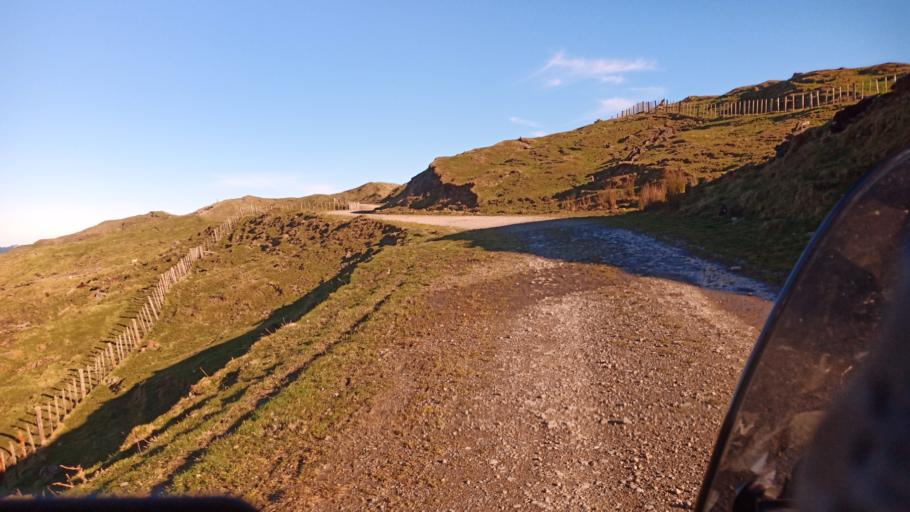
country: NZ
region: Gisborne
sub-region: Gisborne District
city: Gisborne
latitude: -38.1314
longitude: 177.8671
